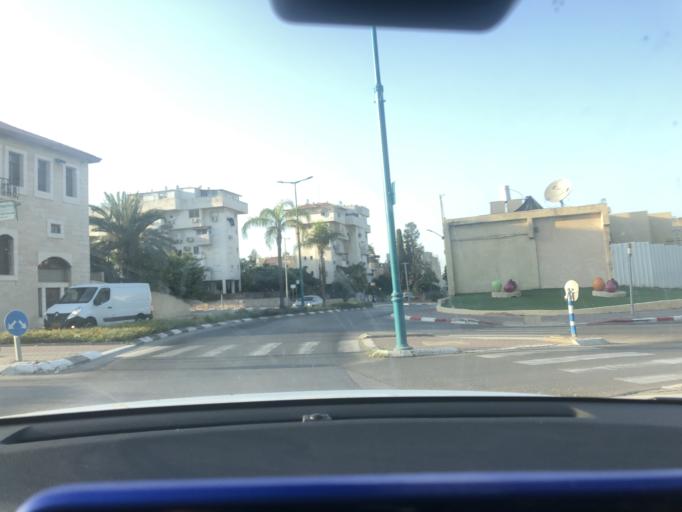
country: IL
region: Central District
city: Lod
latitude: 31.9499
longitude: 34.8955
